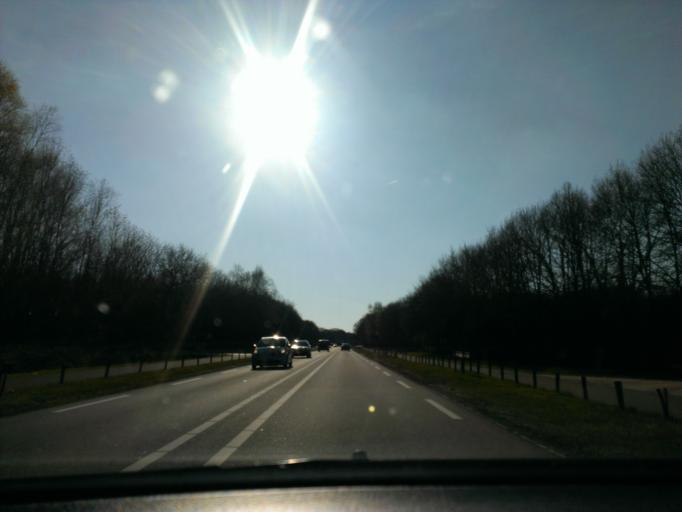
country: NL
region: Overijssel
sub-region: Gemeente Dalfsen
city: Dalfsen
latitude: 52.5278
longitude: 6.3678
